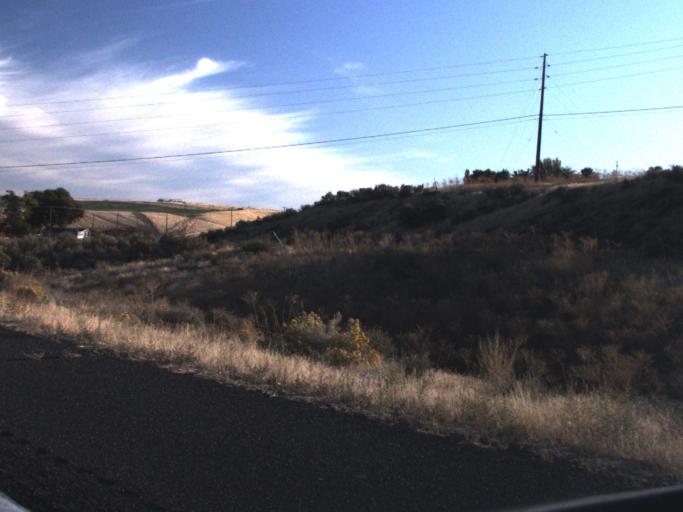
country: US
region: Washington
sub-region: Franklin County
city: Basin City
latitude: 46.4582
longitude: -119.0134
